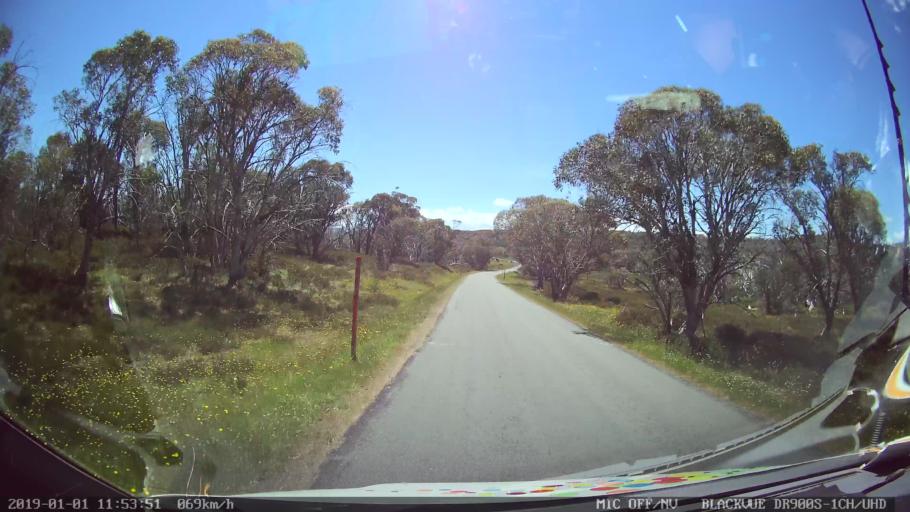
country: AU
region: New South Wales
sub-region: Snowy River
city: Jindabyne
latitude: -35.8921
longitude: 148.4437
